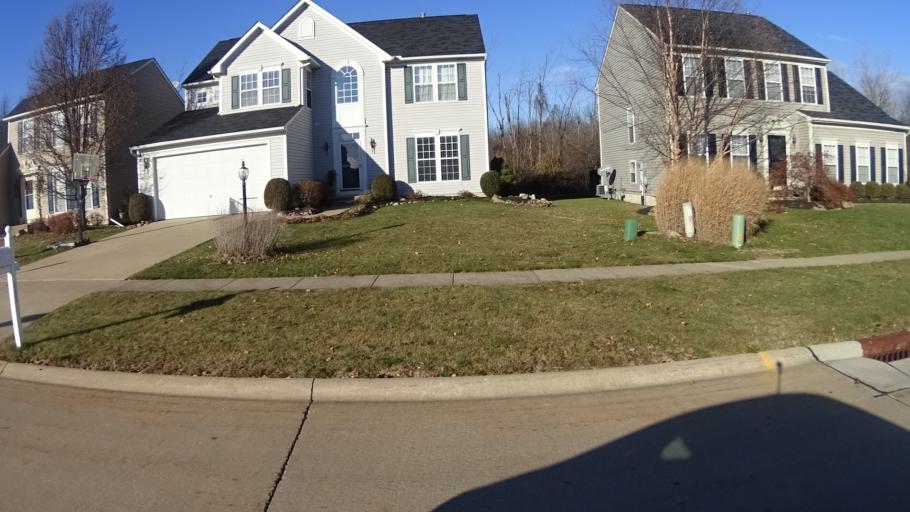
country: US
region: Ohio
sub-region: Lorain County
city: North Ridgeville
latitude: 41.4103
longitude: -82.0447
